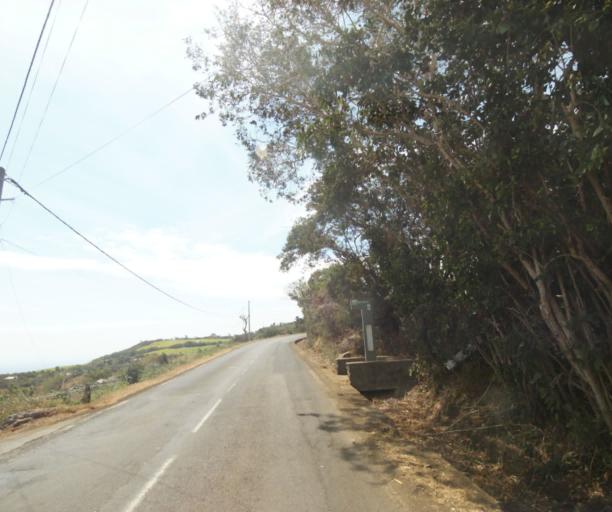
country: RE
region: Reunion
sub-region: Reunion
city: Trois-Bassins
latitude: -21.0969
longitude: 55.2706
